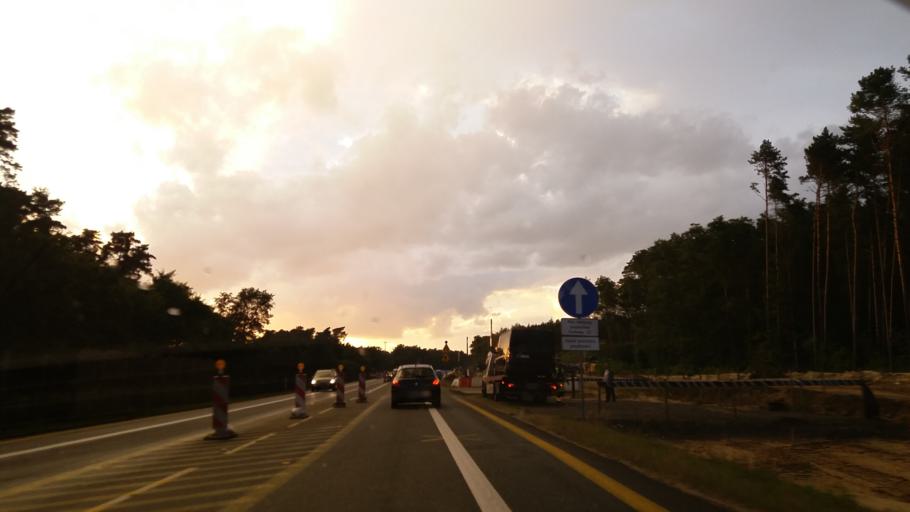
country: PL
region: Lubusz
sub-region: Zielona Gora
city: Zielona Gora
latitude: 51.8967
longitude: 15.6030
